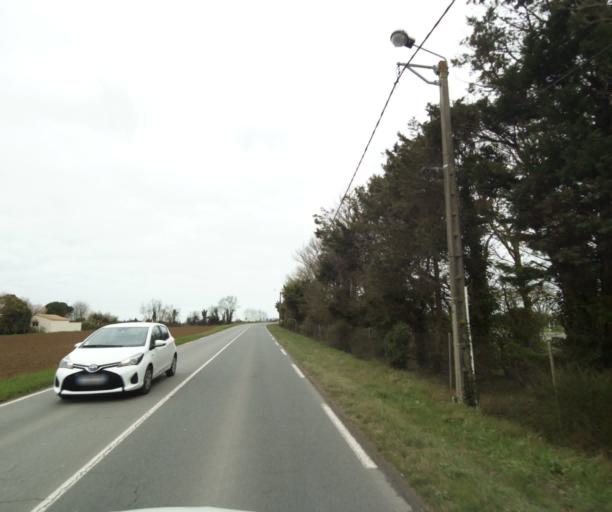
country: FR
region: Poitou-Charentes
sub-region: Departement de la Charente-Maritime
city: Lagord
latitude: 46.1954
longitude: -1.1551
